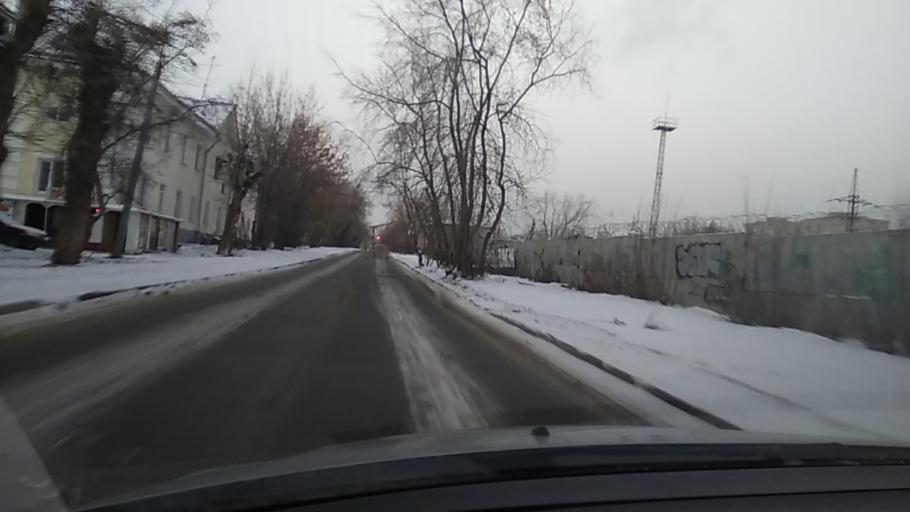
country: RU
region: Sverdlovsk
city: Istok
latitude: 56.7594
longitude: 60.7118
